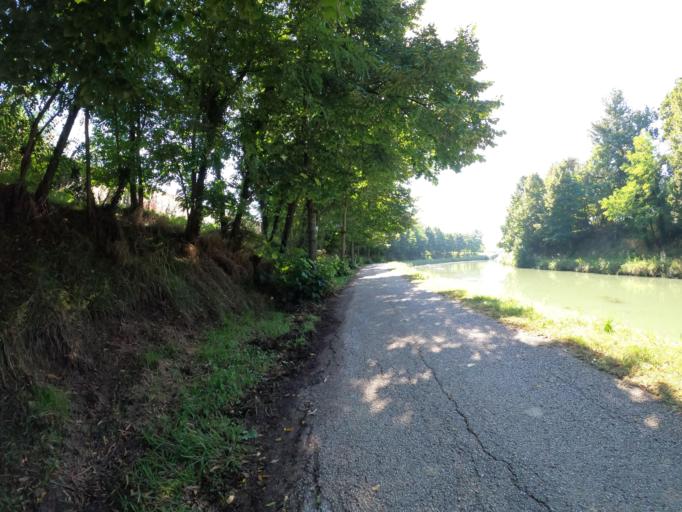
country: FR
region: Aquitaine
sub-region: Departement du Lot-et-Garonne
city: Bon-Encontre
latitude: 44.1924
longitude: 0.6525
